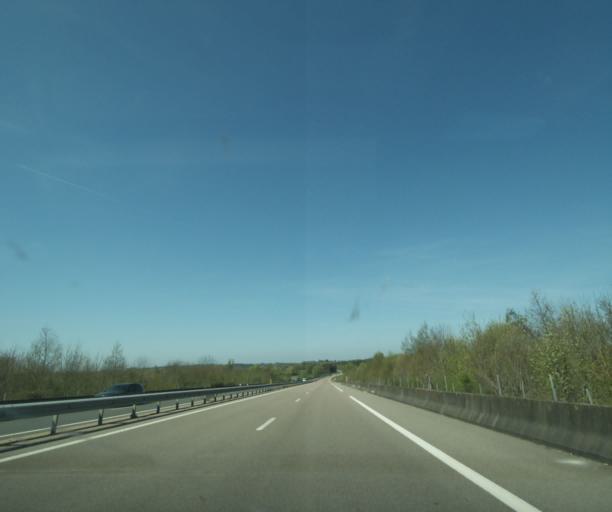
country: FR
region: Bourgogne
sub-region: Departement de la Nievre
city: Pougues-les-Eaux
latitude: 47.0862
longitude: 3.1077
